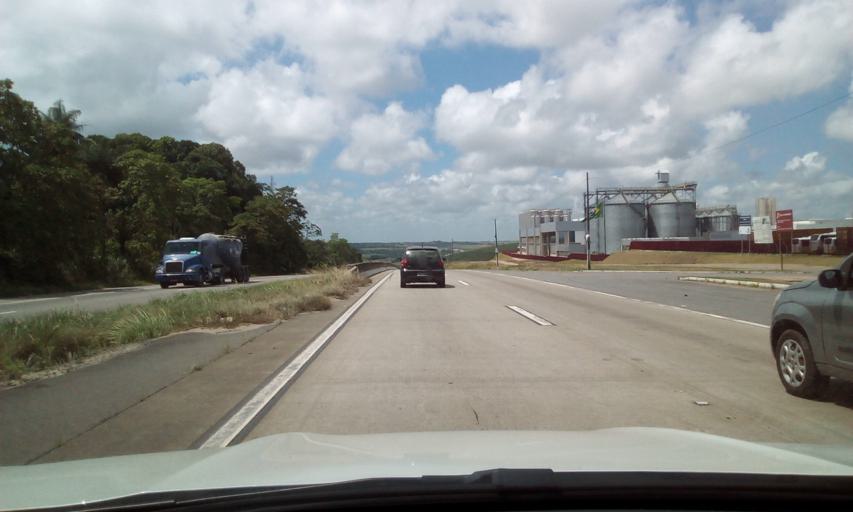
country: BR
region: Pernambuco
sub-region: Itapissuma
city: Itapissuma
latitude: -7.7921
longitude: -34.9288
